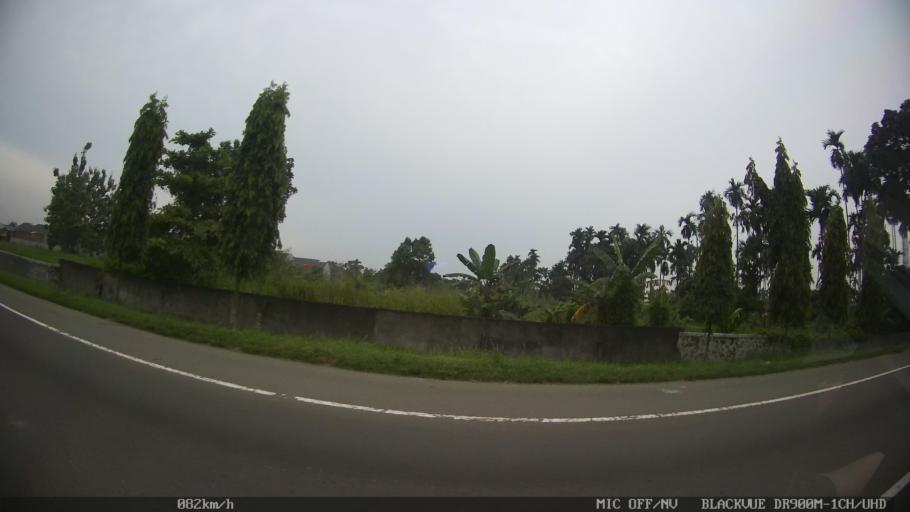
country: ID
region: North Sumatra
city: Medan
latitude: 3.5639
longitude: 98.7258
